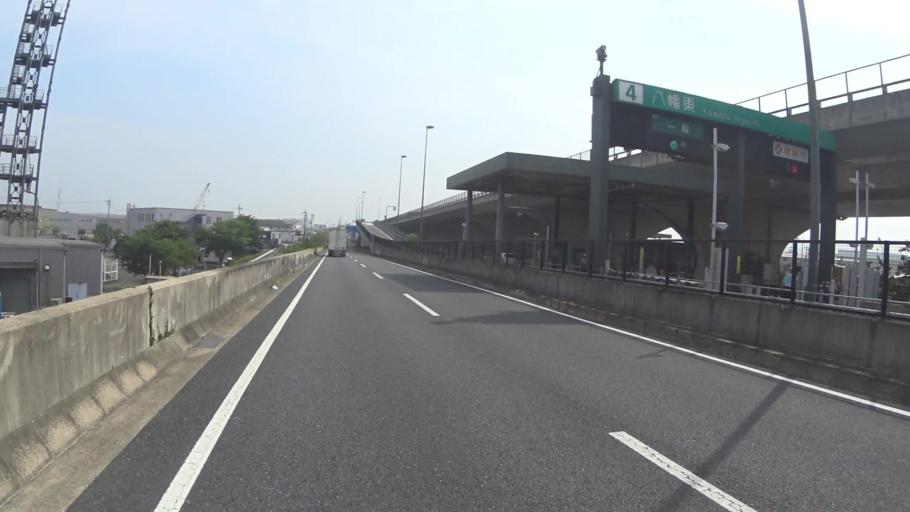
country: JP
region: Kyoto
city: Yawata
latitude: 34.8653
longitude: 135.7368
